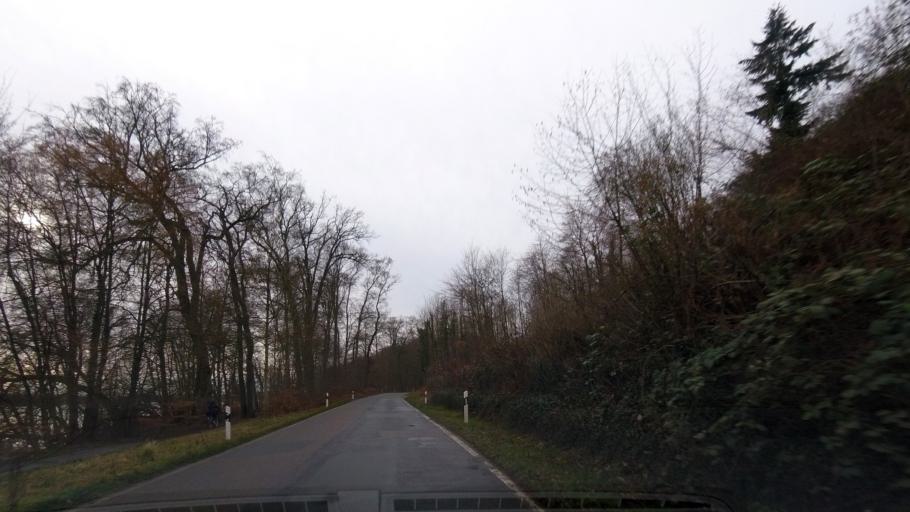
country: DE
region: Mecklenburg-Vorpommern
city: Waren
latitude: 53.5404
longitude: 12.6880
